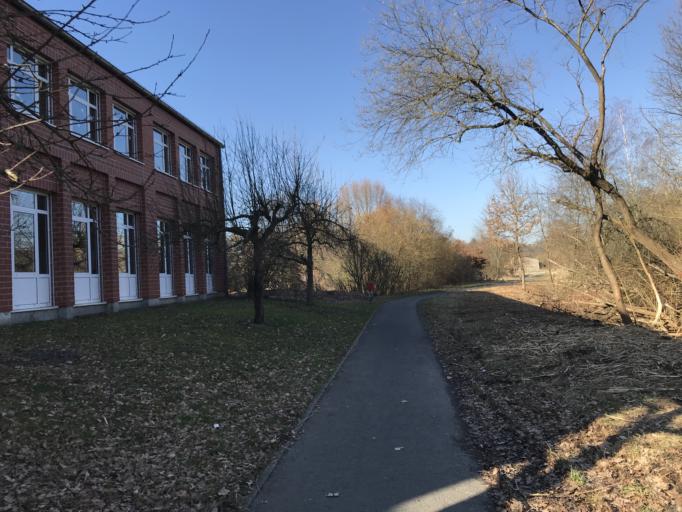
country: DE
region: Hesse
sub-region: Regierungsbezirk Darmstadt
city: Nidda
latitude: 50.4200
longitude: 9.0127
